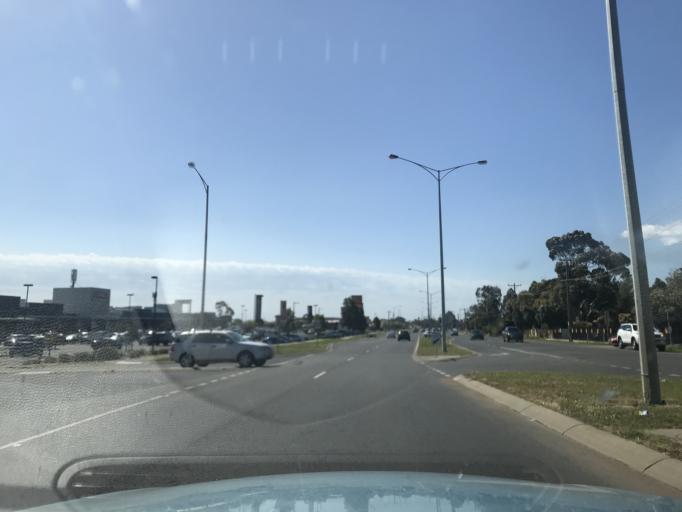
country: AU
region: Victoria
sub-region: Wyndham
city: Hoppers Crossing
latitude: -37.8500
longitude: 144.7026
